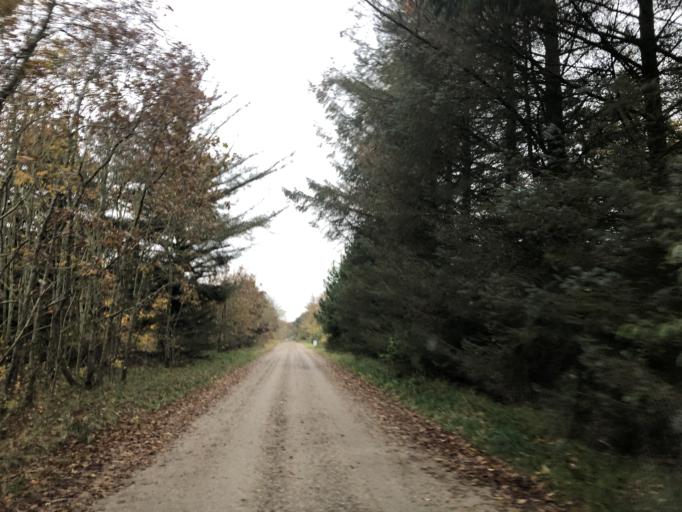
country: DK
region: Central Jutland
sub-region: Holstebro Kommune
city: Ulfborg
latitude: 56.3150
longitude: 8.2114
